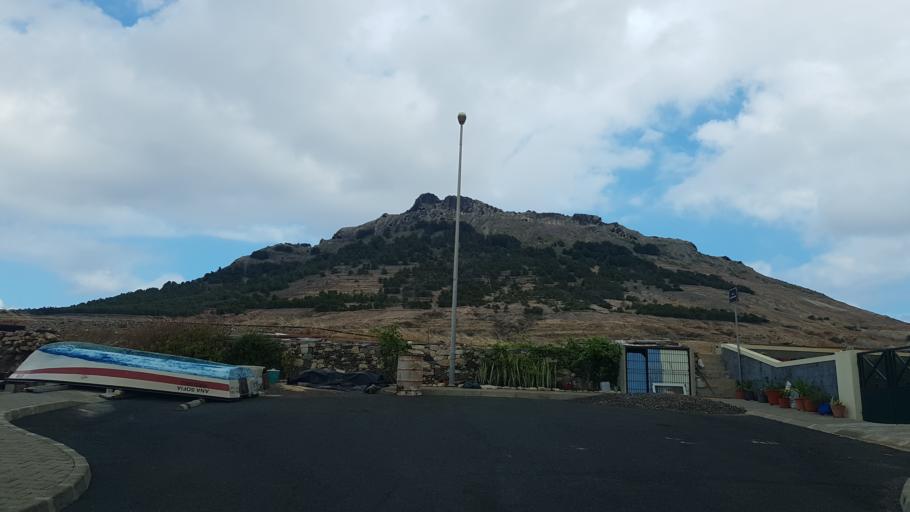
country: PT
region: Madeira
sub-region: Porto Santo
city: Vila de Porto Santo
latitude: 33.0411
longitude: -16.3617
